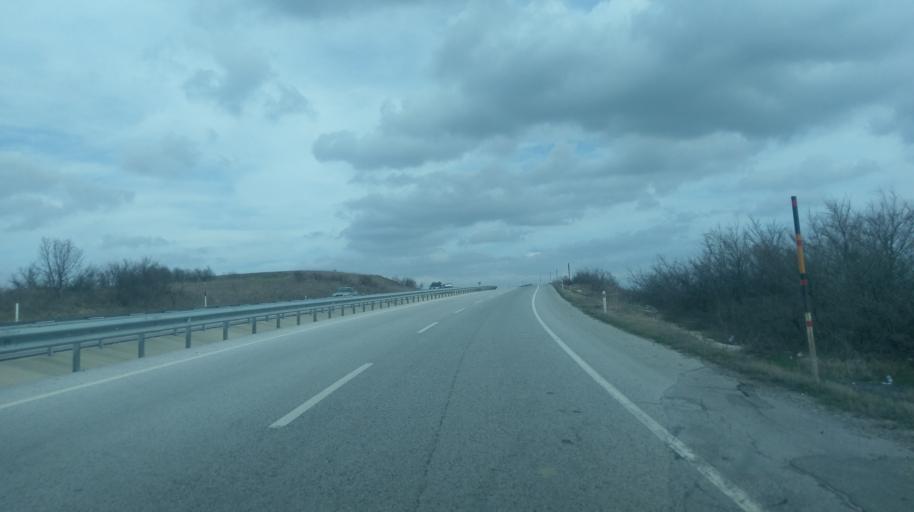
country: TR
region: Edirne
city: Uzun Keupru
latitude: 41.3059
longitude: 26.7101
